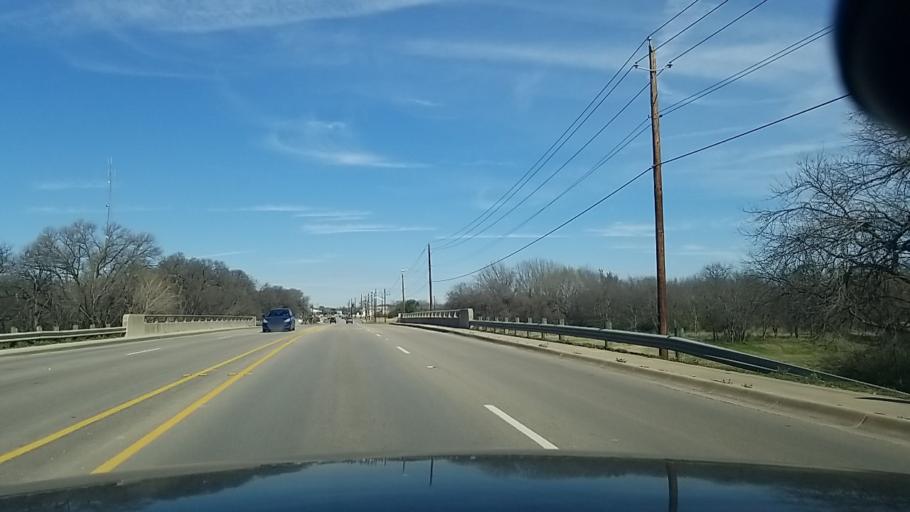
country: US
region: Texas
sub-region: Denton County
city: Denton
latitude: 33.2081
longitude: -97.1120
